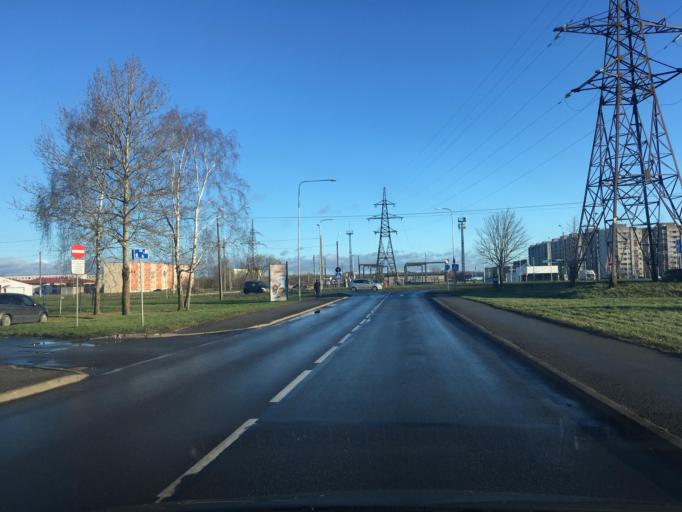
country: EE
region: Ida-Virumaa
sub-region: Narva linn
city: Narva
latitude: 59.3872
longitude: 28.1737
